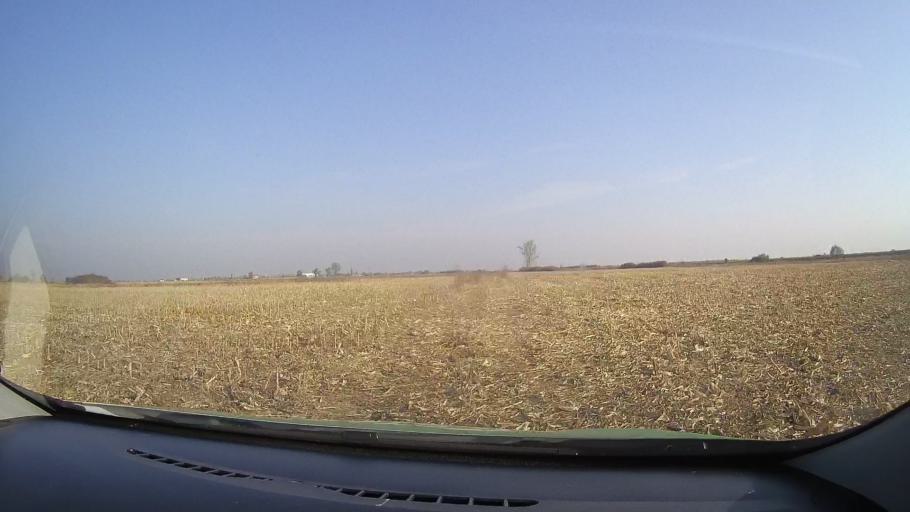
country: RO
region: Arad
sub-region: Comuna Pilu
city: Pilu
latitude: 46.5587
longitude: 21.3450
